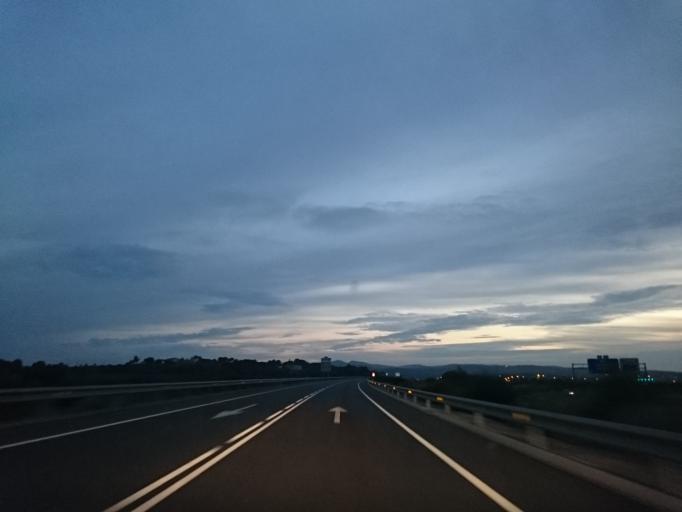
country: ES
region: Catalonia
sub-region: Provincia de Barcelona
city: Vilafranca del Penedes
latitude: 41.3399
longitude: 1.7181
